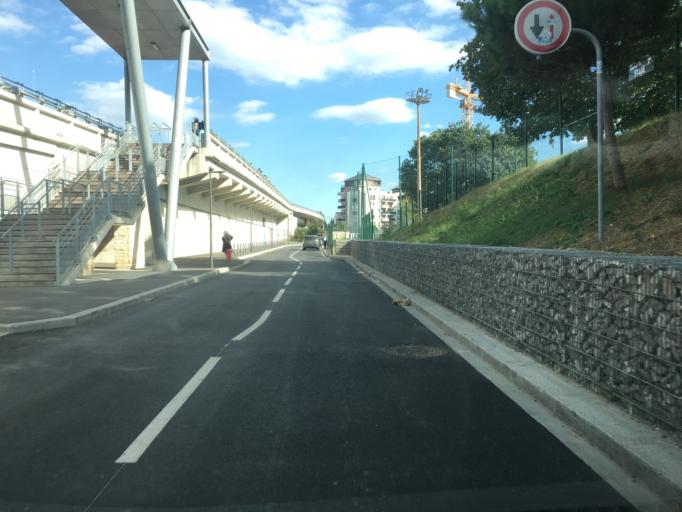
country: FR
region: Ile-de-France
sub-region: Departement du Val-de-Marne
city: Creteil
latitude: 48.7688
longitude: 2.4627
